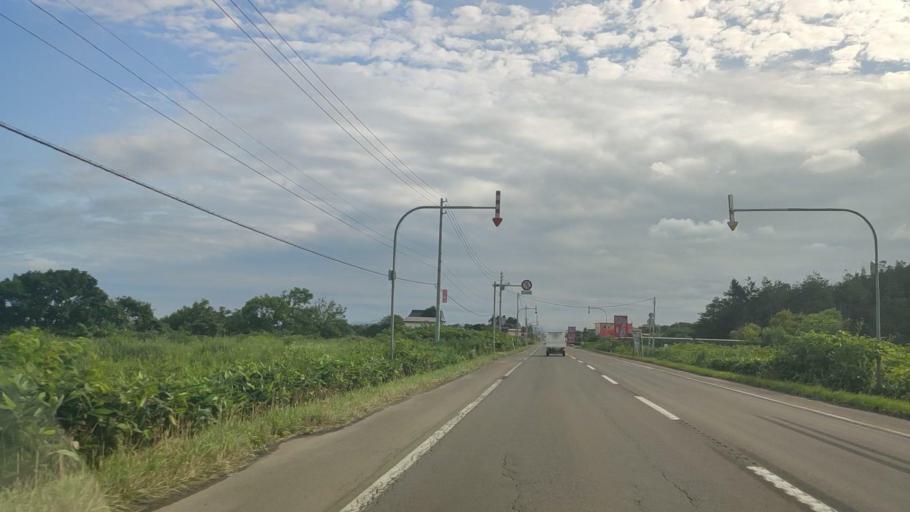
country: JP
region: Hokkaido
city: Niseko Town
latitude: 42.4811
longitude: 140.3506
